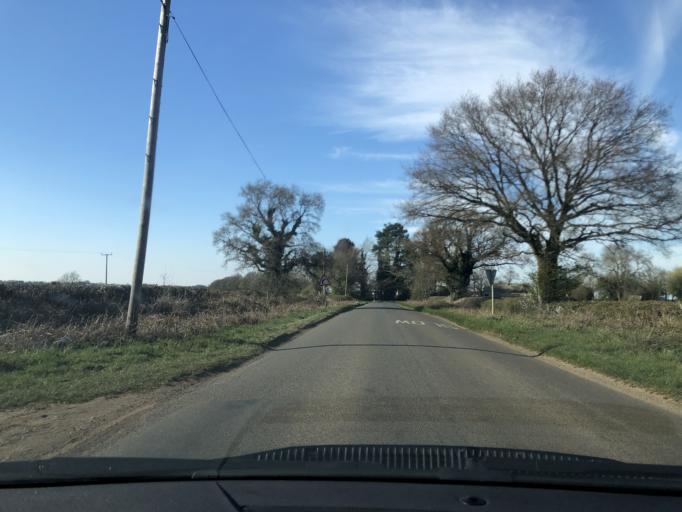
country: GB
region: England
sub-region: Oxfordshire
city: Hook Norton
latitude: 52.0146
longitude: -1.4406
